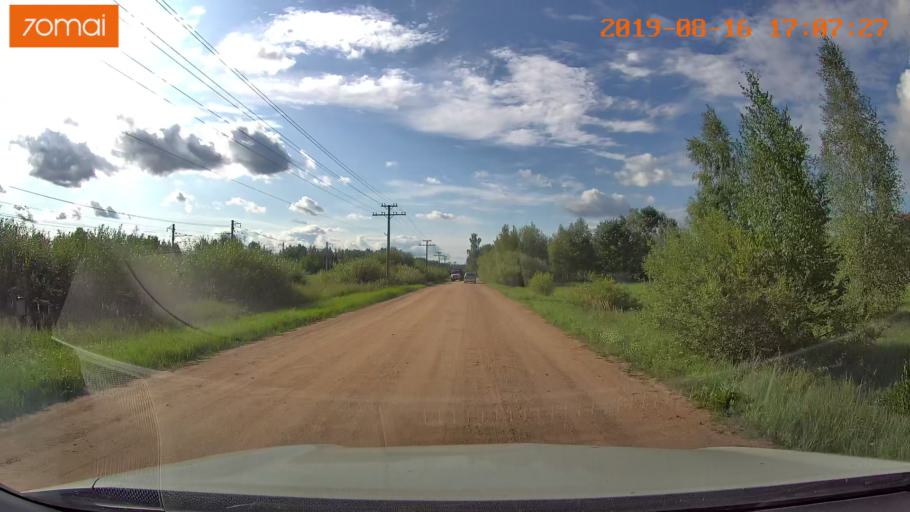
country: BY
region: Mogilev
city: Hlusha
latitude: 53.2213
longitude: 28.9243
